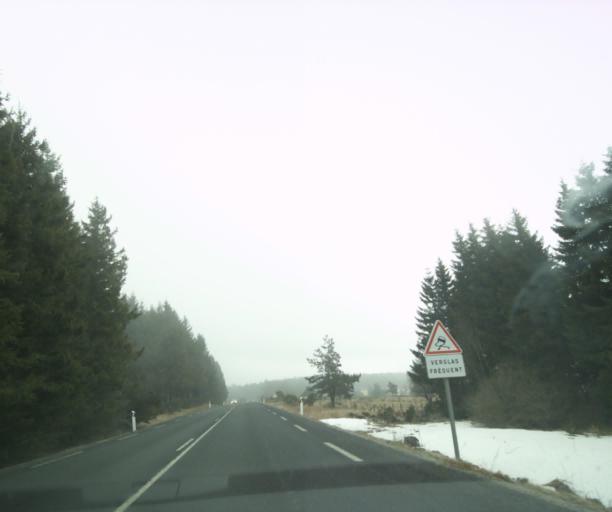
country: FR
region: Languedoc-Roussillon
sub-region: Departement de la Lozere
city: Langogne
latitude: 44.7516
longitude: 3.9487
